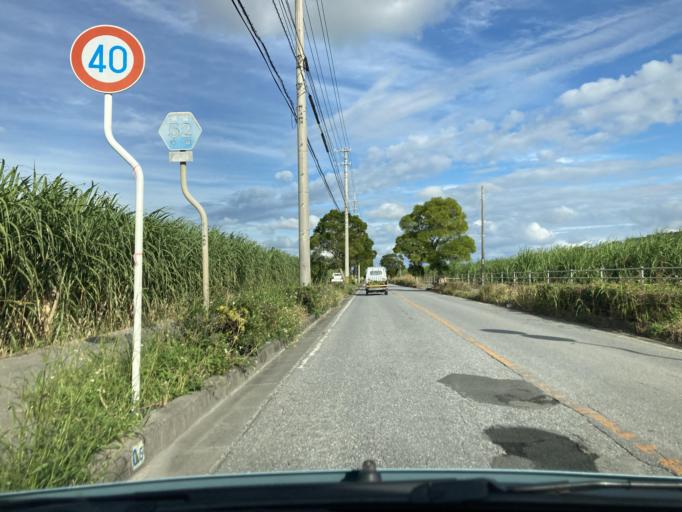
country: JP
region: Okinawa
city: Itoman
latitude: 26.1346
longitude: 127.7013
